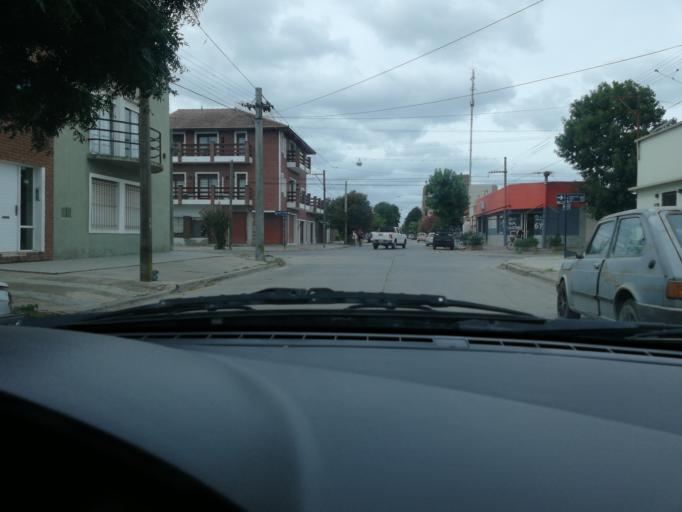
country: AR
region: Buenos Aires
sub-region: Partido de Balcarce
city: Balcarce
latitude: -37.8463
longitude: -58.2617
